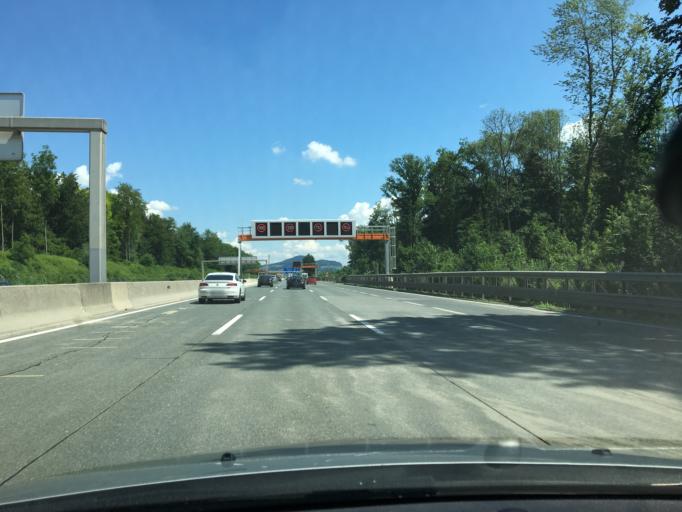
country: DE
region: Bavaria
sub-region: Upper Bavaria
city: Ainring
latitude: 47.7973
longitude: 12.9867
